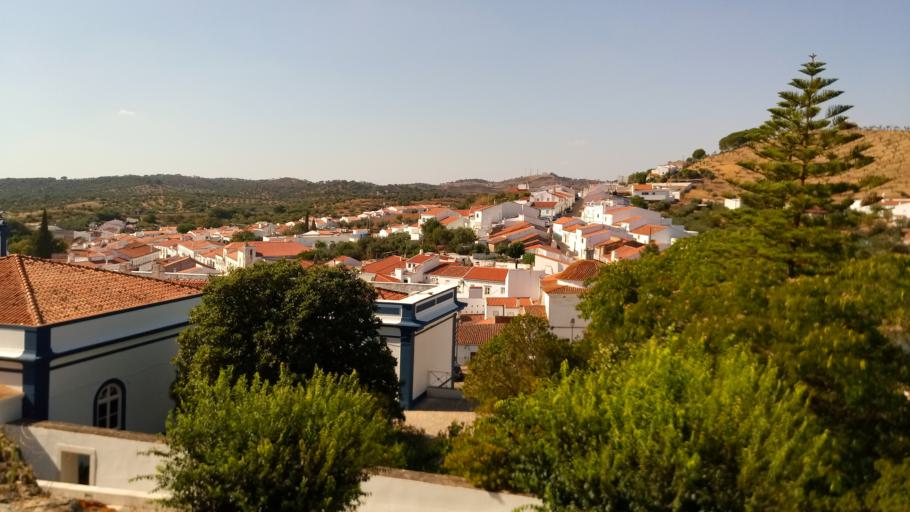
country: PT
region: Evora
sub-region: Portel
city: Portel
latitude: 38.3094
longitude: -7.7025
